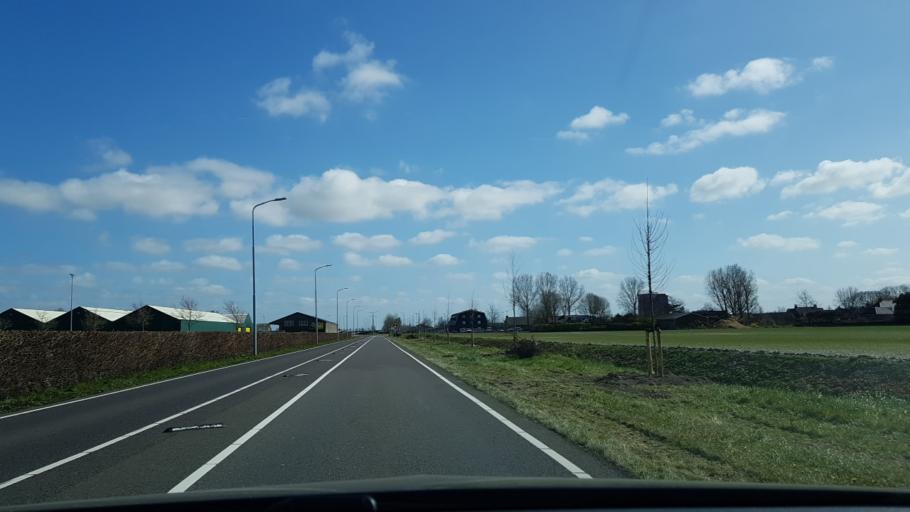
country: NL
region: South Holland
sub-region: Gemeente Hillegom
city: Hillegom
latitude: 52.2869
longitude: 4.6195
